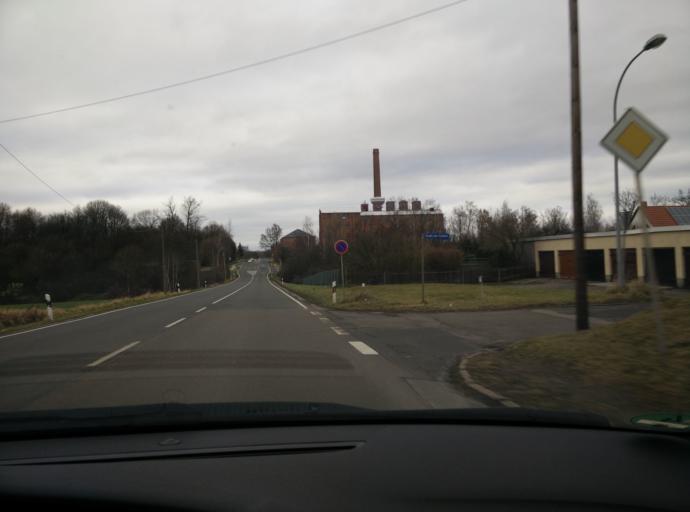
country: DE
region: Saxony
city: Frohburg
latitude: 51.0882
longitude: 12.5296
